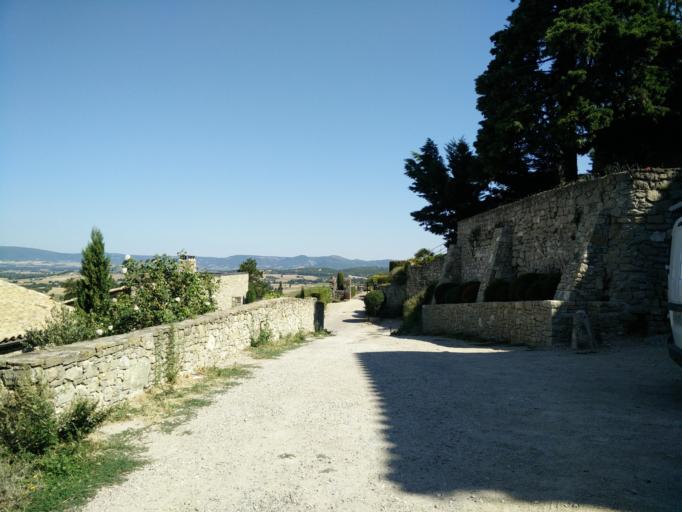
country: FR
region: Rhone-Alpes
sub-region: Departement de la Drome
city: La Begude-de-Mazenc
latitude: 44.5519
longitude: 4.9380
